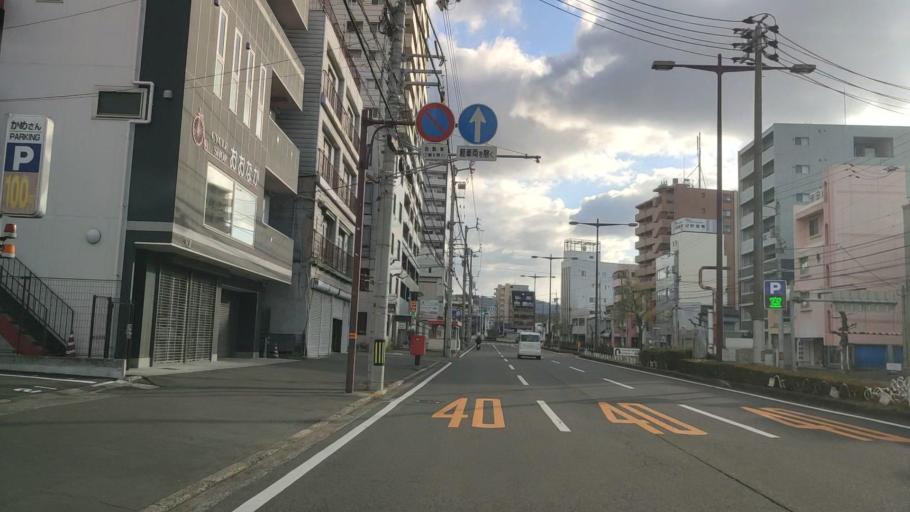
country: JP
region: Ehime
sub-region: Shikoku-chuo Shi
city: Matsuyama
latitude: 33.8351
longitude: 132.7684
